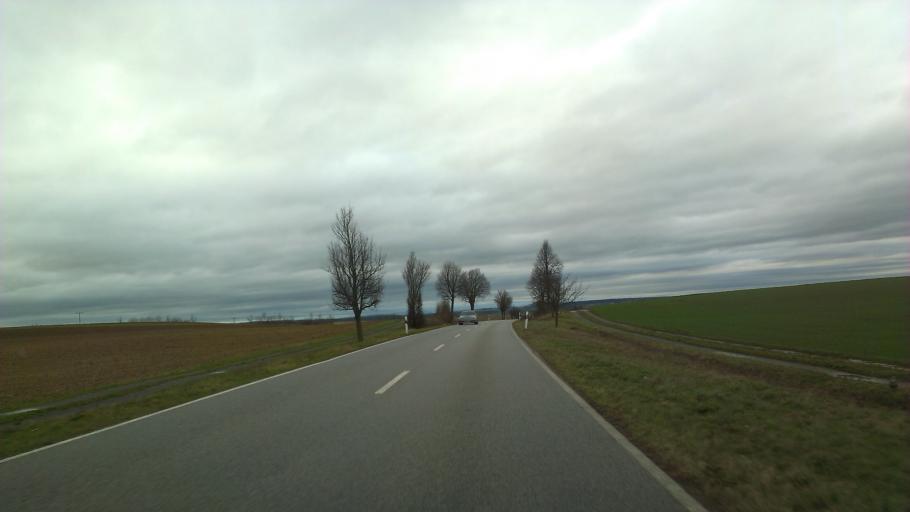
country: DE
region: Baden-Wuerttemberg
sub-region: Regierungsbezirk Stuttgart
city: Eppingen
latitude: 49.1121
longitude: 8.8986
